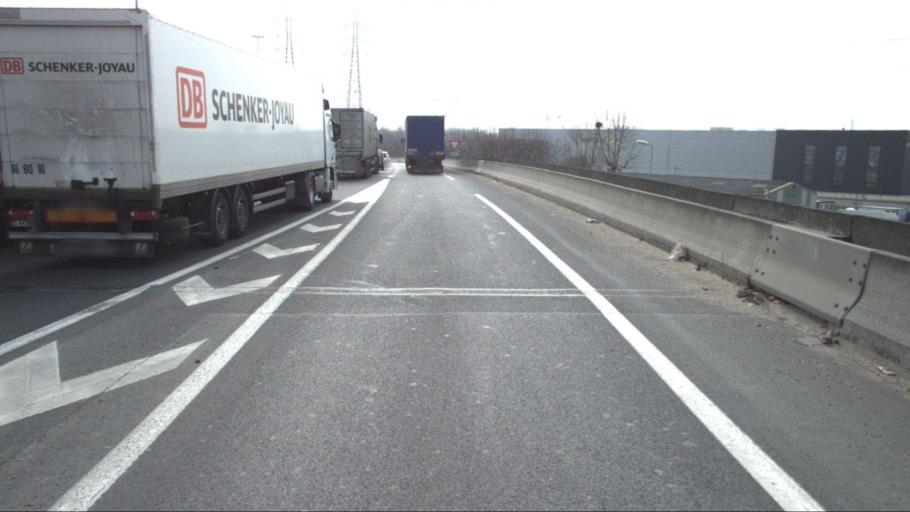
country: FR
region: Ile-de-France
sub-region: Departement des Hauts-de-Seine
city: Villeneuve-la-Garenne
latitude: 48.9320
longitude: 2.3220
